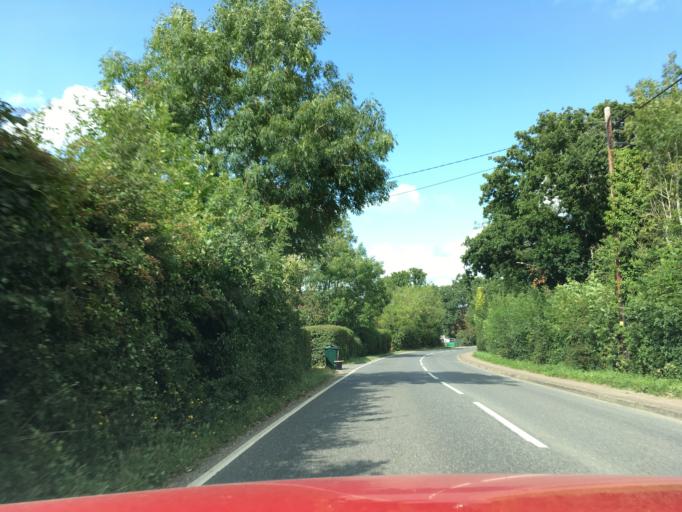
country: GB
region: England
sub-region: Kent
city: Headcorn
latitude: 51.1187
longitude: 0.6439
